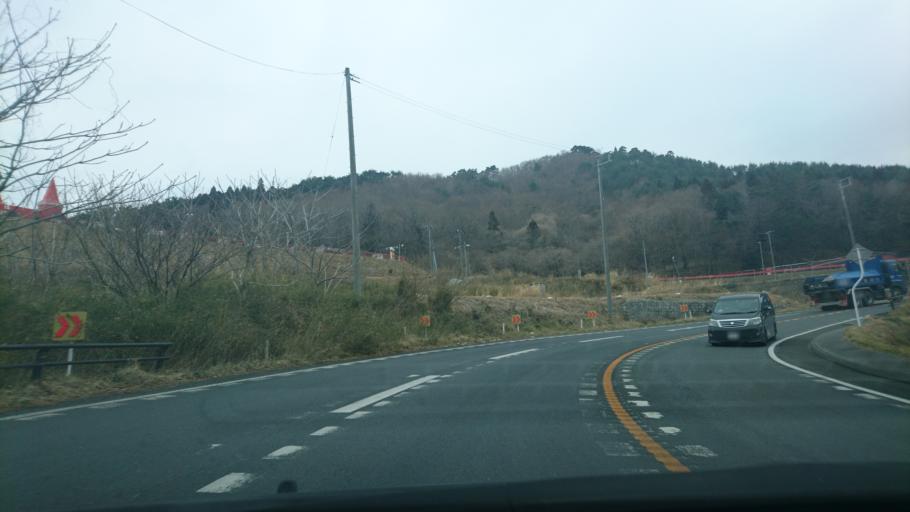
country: JP
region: Iwate
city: Ofunato
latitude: 39.0249
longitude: 141.6901
